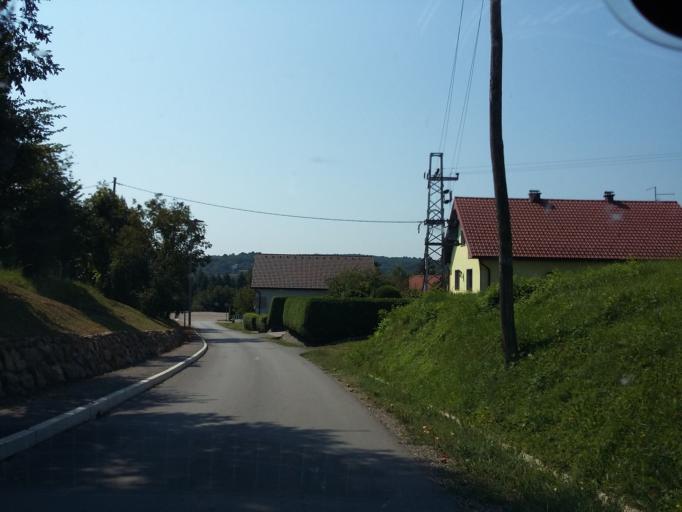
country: SI
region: Hodos-Hodos
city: Hodos
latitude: 46.8227
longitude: 16.3255
